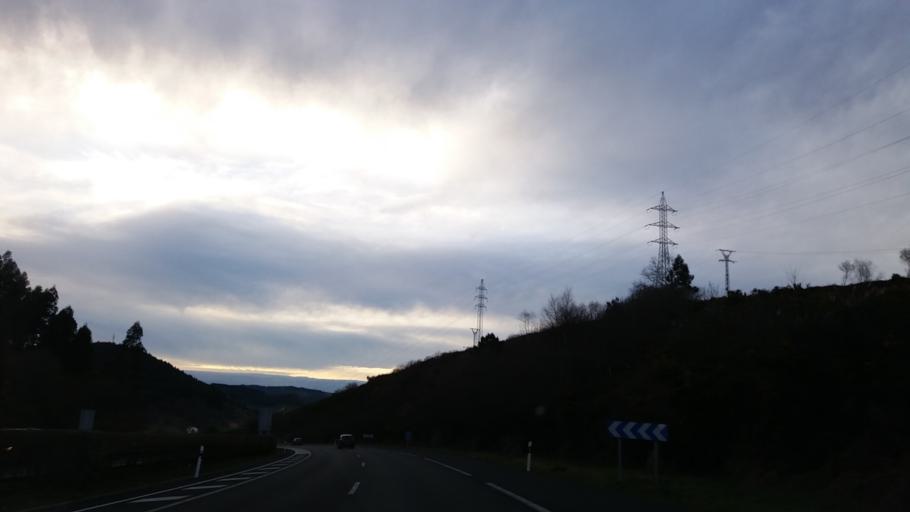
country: ES
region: Cantabria
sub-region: Provincia de Cantabria
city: Barcena de Cicero
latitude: 43.4097
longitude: -3.5002
